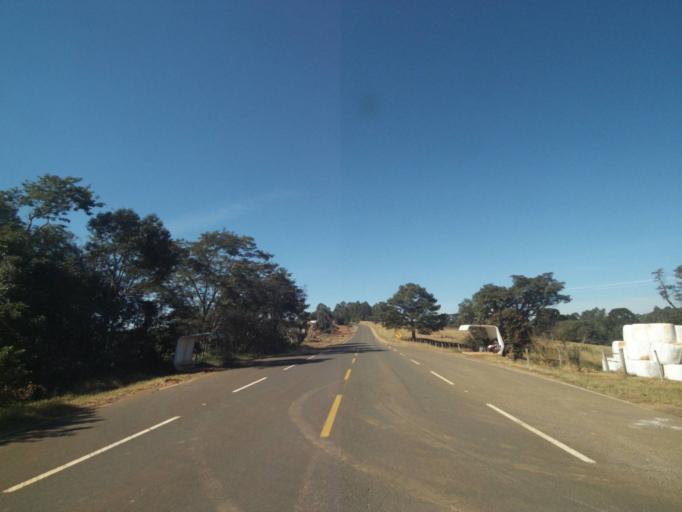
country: BR
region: Parana
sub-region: Tibagi
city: Tibagi
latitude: -24.4812
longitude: -50.4783
